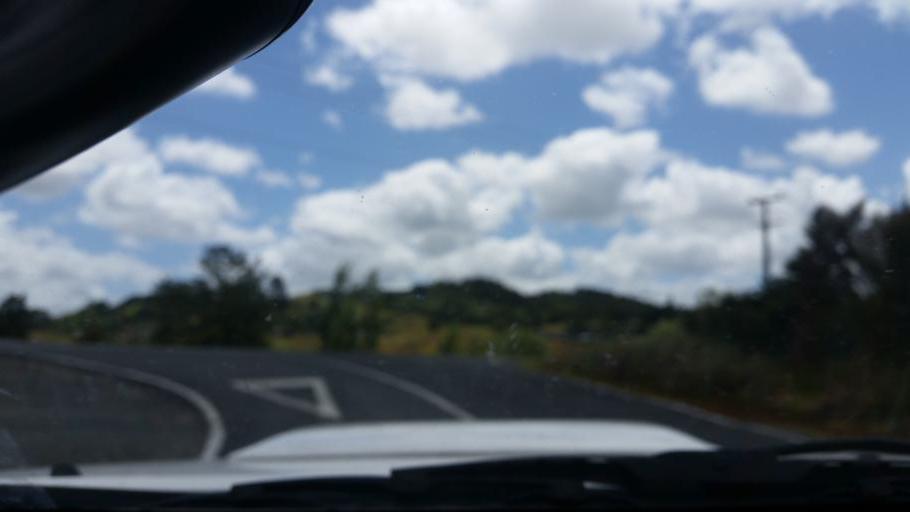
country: NZ
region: Northland
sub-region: Whangarei
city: Ruakaka
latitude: -36.0403
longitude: 174.2797
